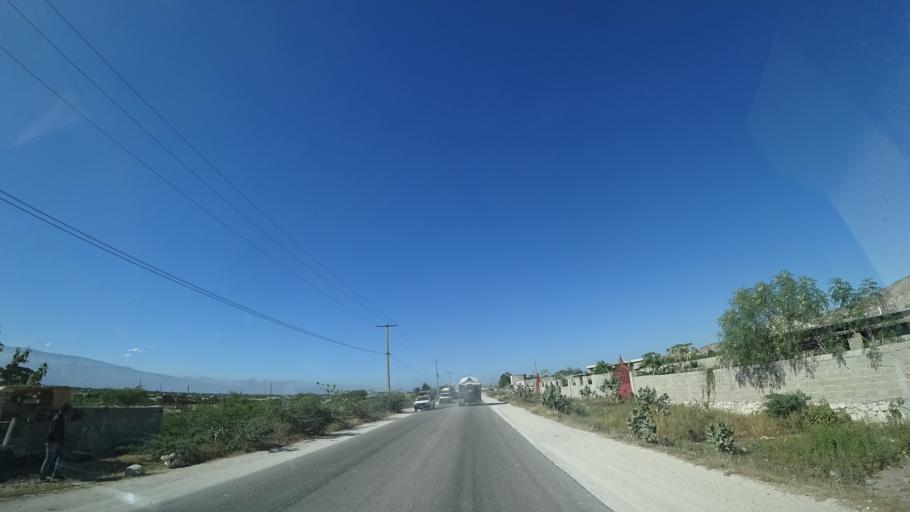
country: HT
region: Ouest
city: Croix des Bouquets
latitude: 18.6489
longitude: -72.2448
